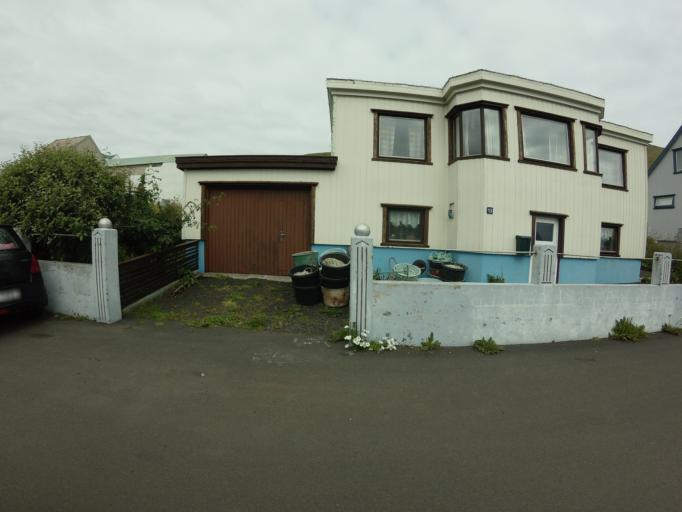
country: FO
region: Suduroy
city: Tvoroyri
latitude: 61.6333
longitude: -6.9269
